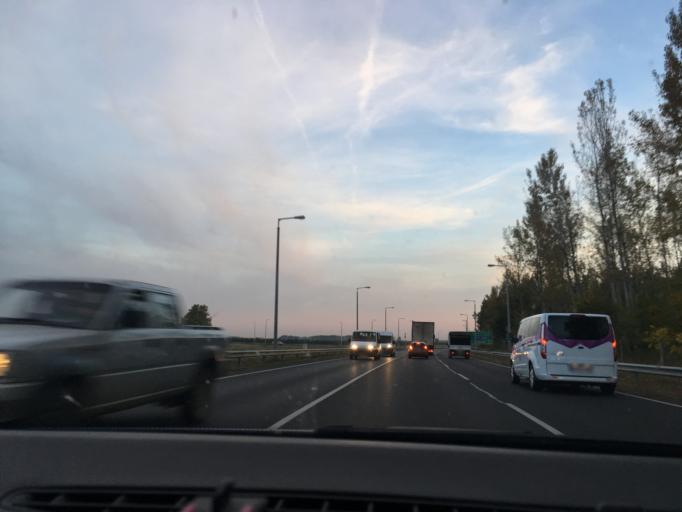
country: HU
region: Hajdu-Bihar
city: Hajduhadhaz
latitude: 47.6678
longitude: 21.6517
